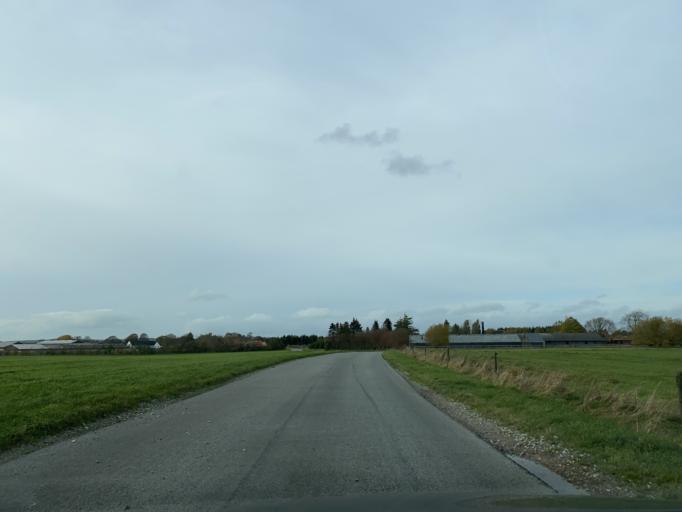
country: DK
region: Central Jutland
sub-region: Arhus Kommune
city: Framlev
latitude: 56.1625
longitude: 9.9995
